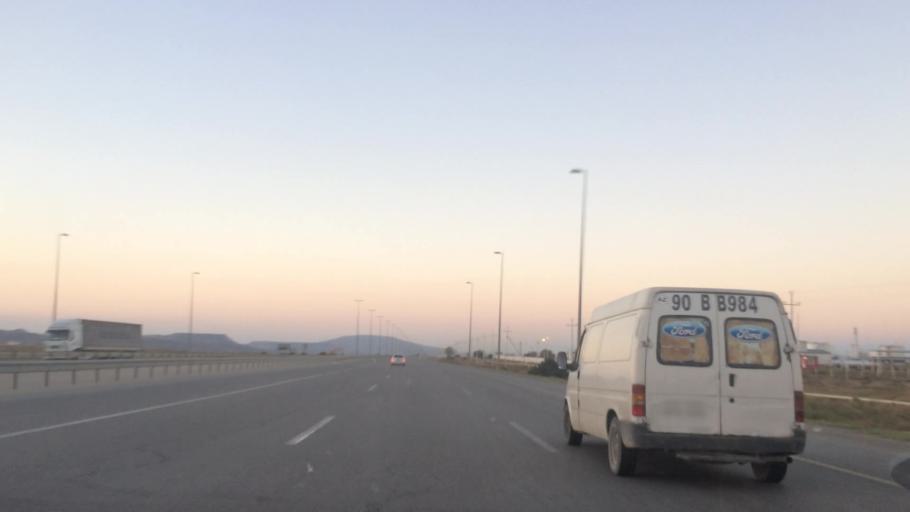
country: AZ
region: Baki
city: Qobustan
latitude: 39.9965
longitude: 49.4307
